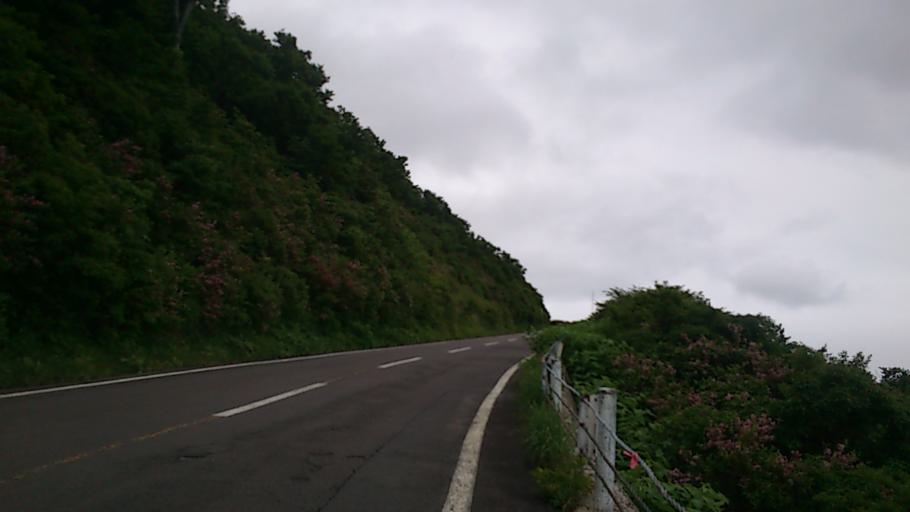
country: JP
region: Yamagata
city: Yuza
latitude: 39.1242
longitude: 139.9877
